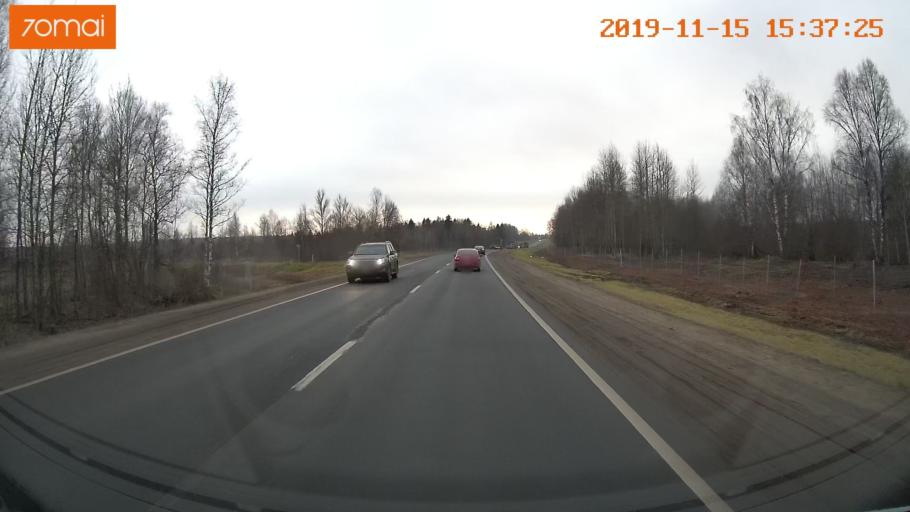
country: RU
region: Jaroslavl
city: Danilov
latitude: 58.0396
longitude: 40.0881
